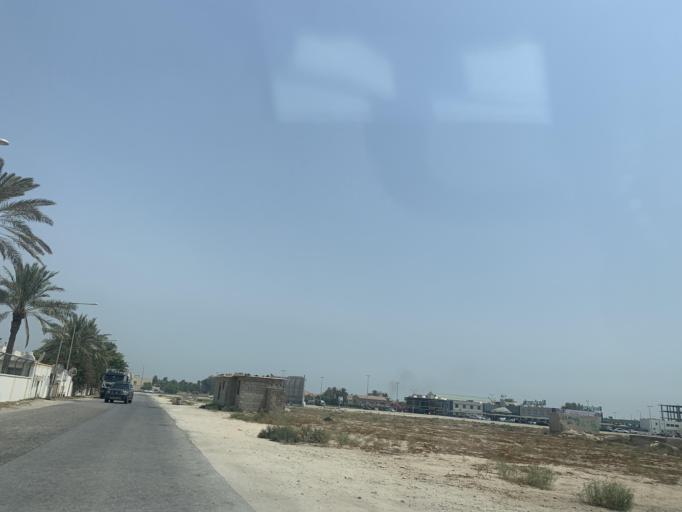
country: BH
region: Manama
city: Jidd Hafs
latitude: 26.2145
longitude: 50.4780
